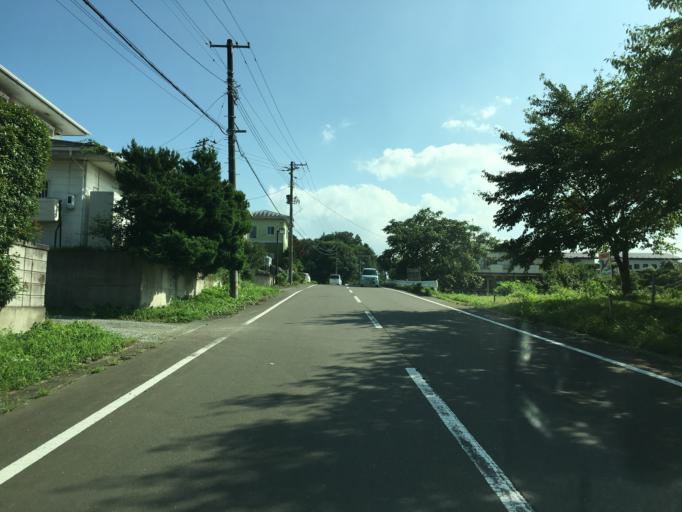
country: JP
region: Miyagi
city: Marumori
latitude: 37.9440
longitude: 140.7732
